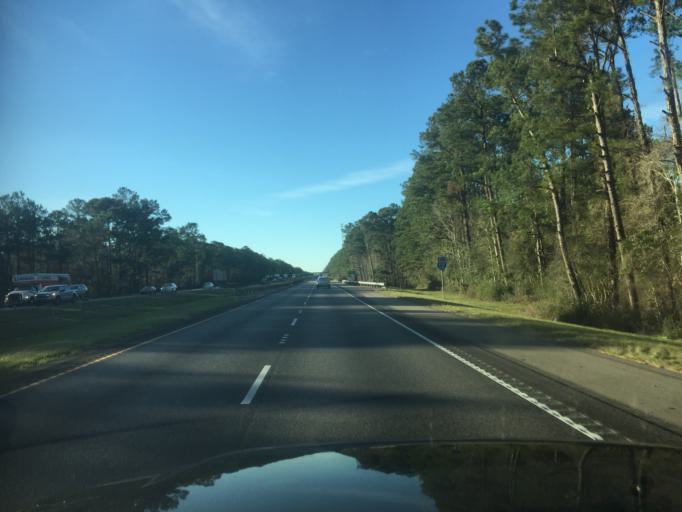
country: US
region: Louisiana
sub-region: Saint Tammany Parish
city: Lacombe
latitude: 30.3564
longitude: -89.9279
